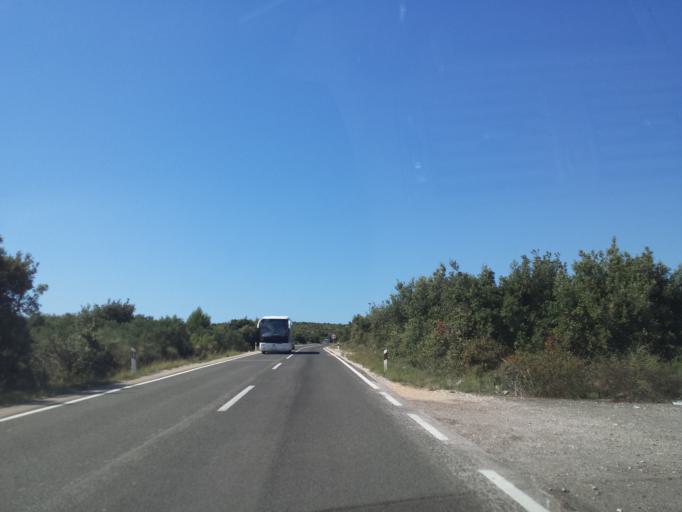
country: HR
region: Sibensko-Kniniska
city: Rogoznica
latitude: 43.5441
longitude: 15.9645
